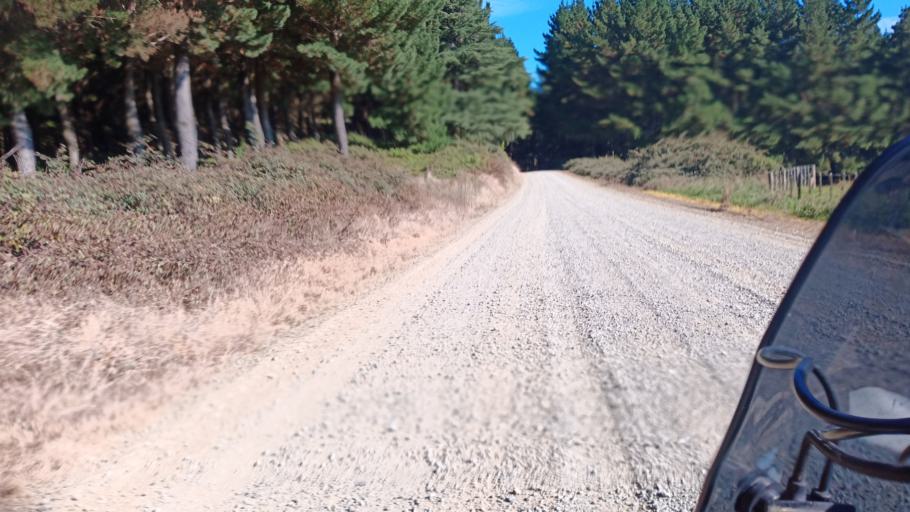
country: NZ
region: Hawke's Bay
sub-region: Wairoa District
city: Wairoa
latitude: -38.9332
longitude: 177.2388
